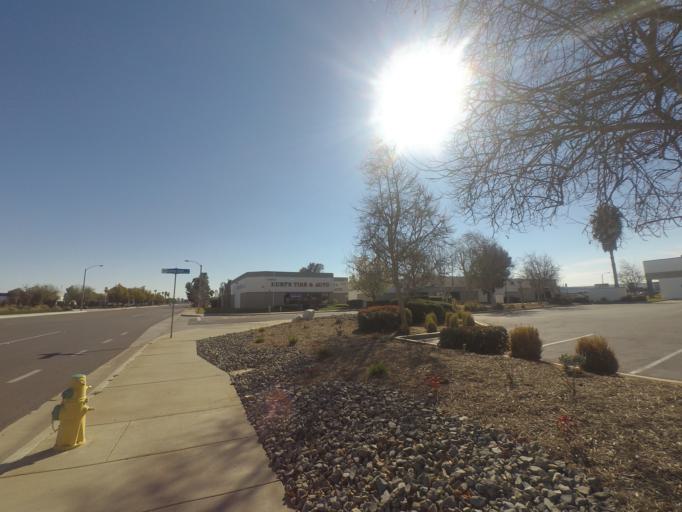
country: US
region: California
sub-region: Riverside County
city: March Air Force Base
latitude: 33.9145
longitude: -117.2702
